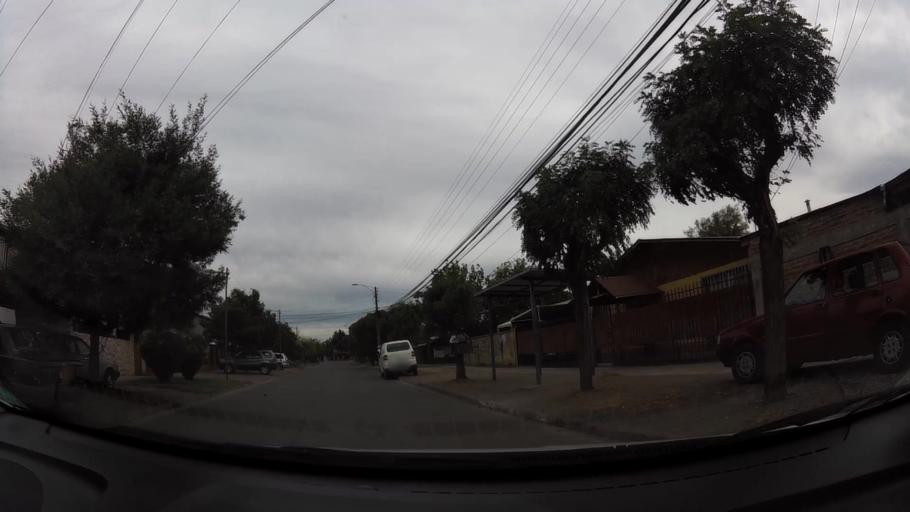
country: CL
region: O'Higgins
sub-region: Provincia de Cachapoal
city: Rancagua
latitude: -34.1494
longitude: -70.7345
